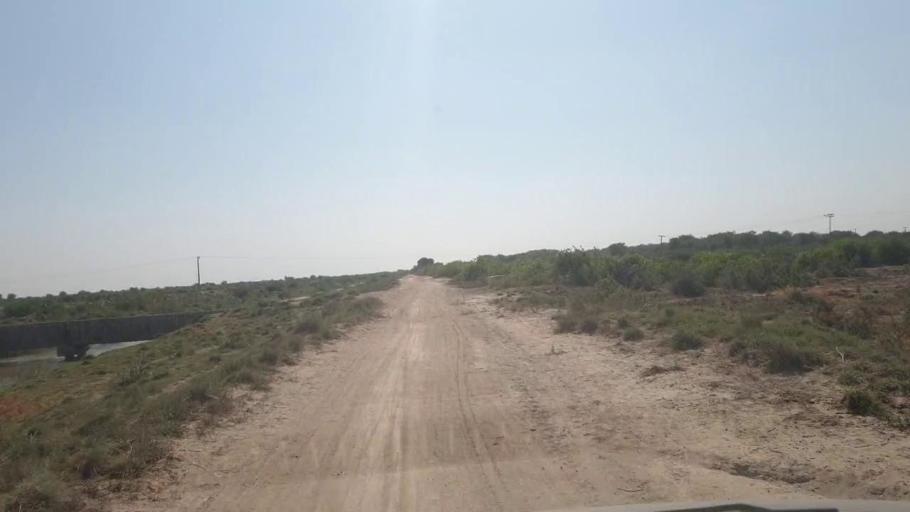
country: PK
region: Sindh
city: Tando Bago
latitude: 24.9193
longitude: 69.1645
